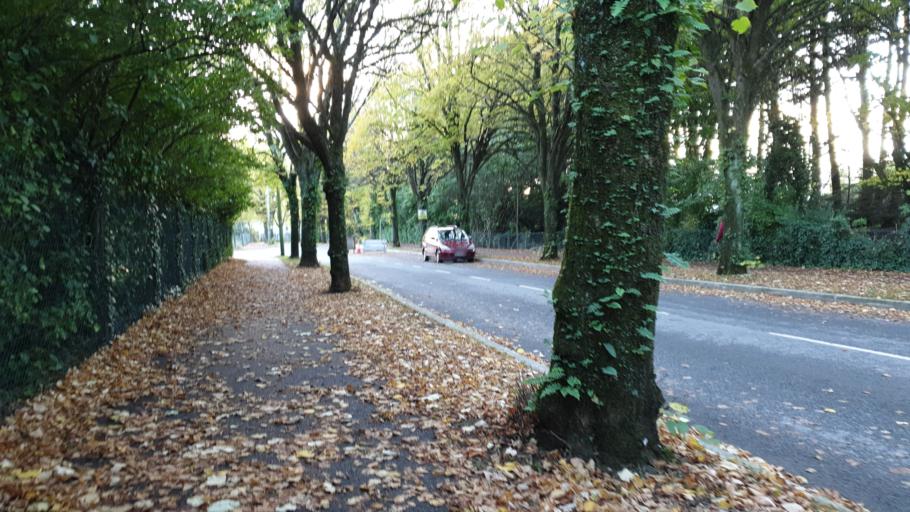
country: IE
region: Munster
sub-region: County Cork
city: Cork
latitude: 51.8994
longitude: -8.4420
